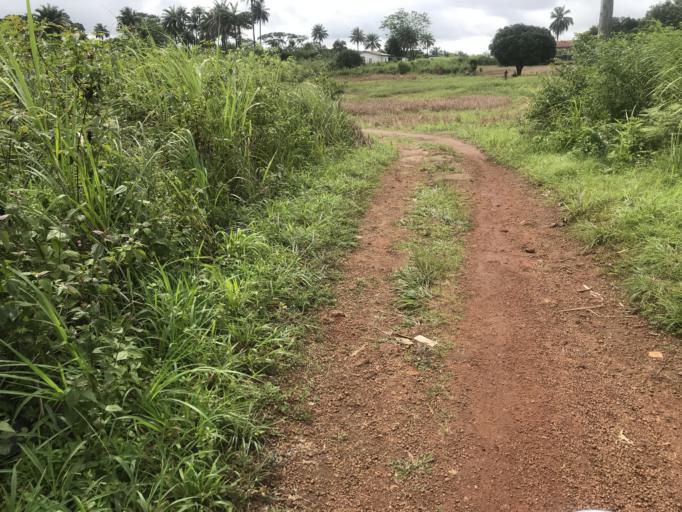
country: SL
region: Eastern Province
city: Buedu
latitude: 8.4626
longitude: -10.3115
